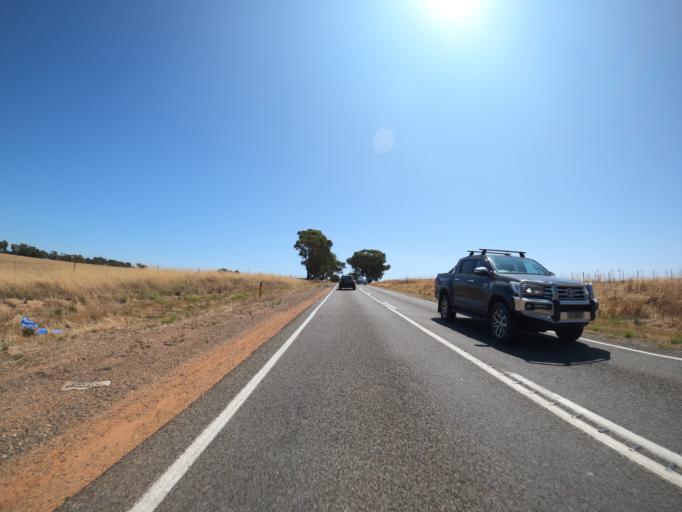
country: AU
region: Victoria
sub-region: Moira
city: Yarrawonga
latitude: -36.0231
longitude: 146.1243
